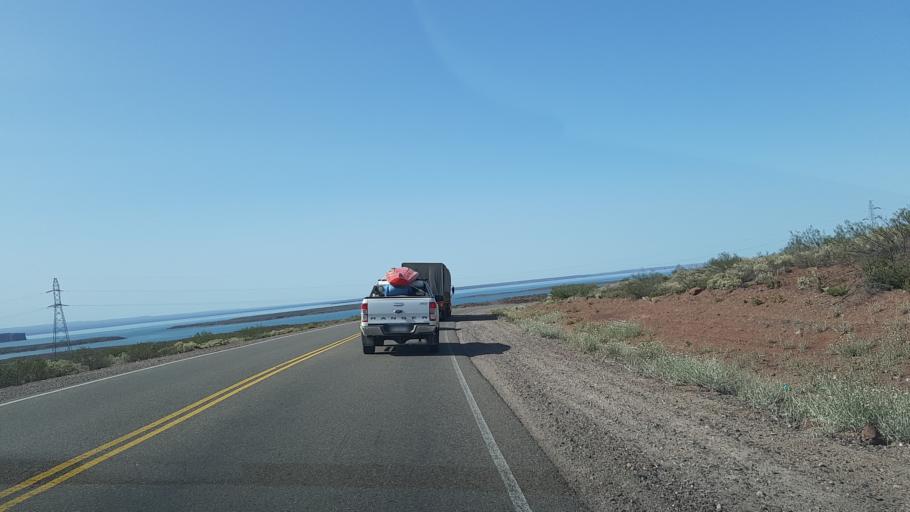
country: AR
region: Neuquen
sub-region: Departamento de Picun Leufu
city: Picun Leufu
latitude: -39.2718
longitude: -68.8543
